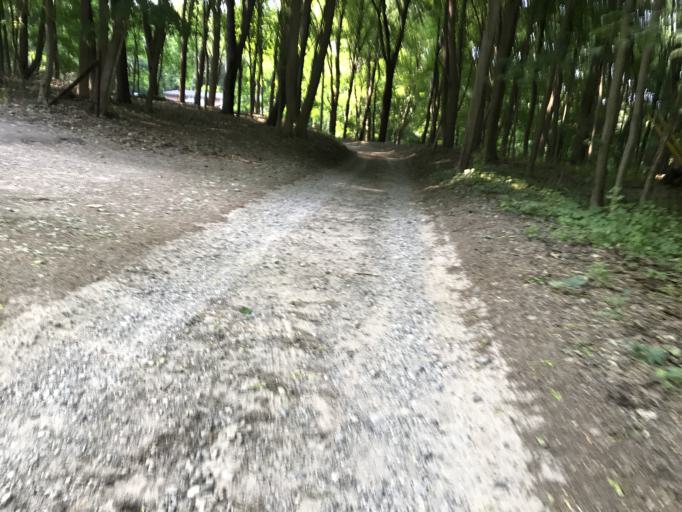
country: US
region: Michigan
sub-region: Oakland County
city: Farmington
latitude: 42.4703
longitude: -83.3839
